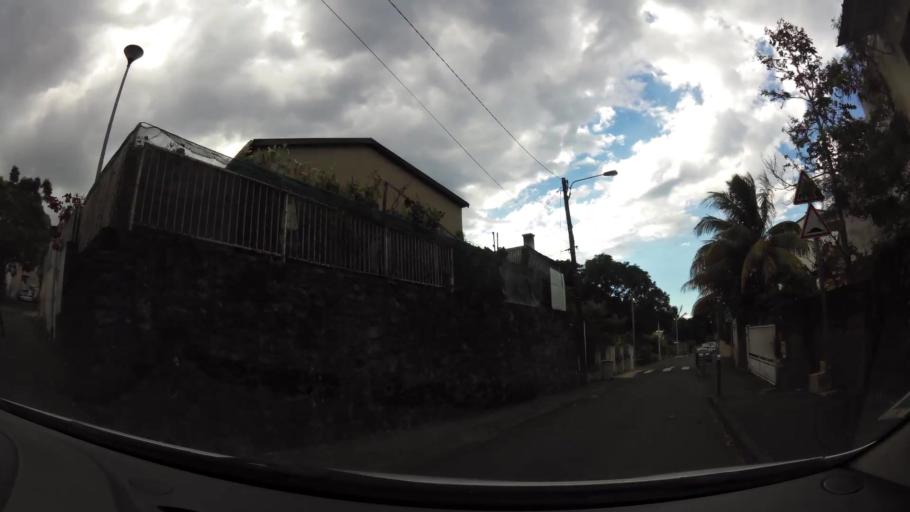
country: RE
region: Reunion
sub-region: Reunion
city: Saint-Denis
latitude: -20.8932
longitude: 55.4785
